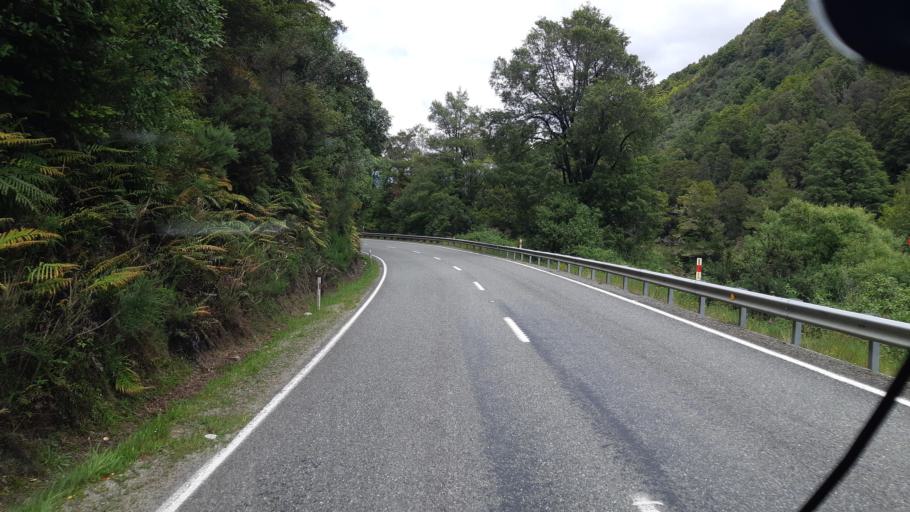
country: NZ
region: West Coast
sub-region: Buller District
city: Westport
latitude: -42.1380
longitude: 171.8888
